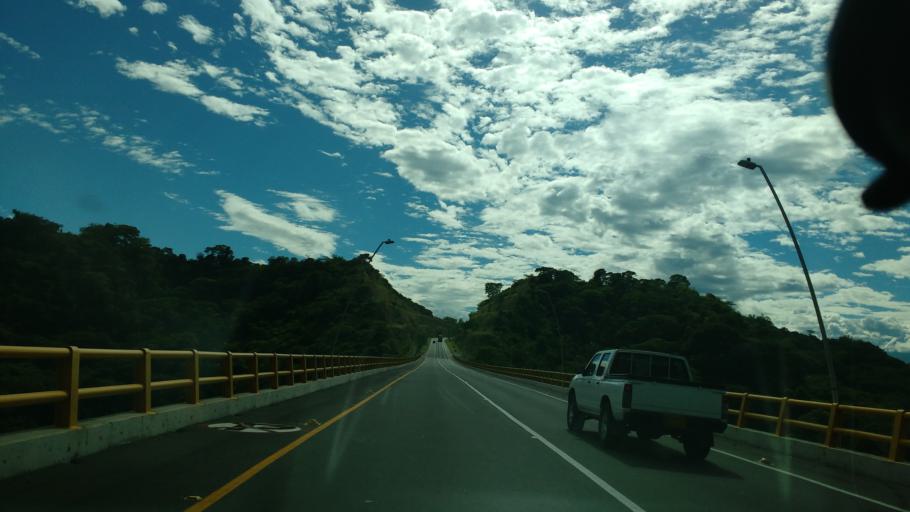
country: CO
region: Tolima
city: Valle de San Juan
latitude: 4.2912
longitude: -75.0348
